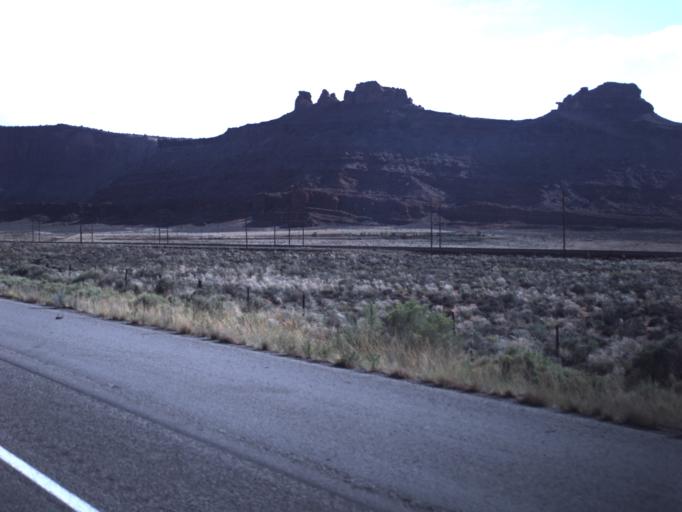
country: US
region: Utah
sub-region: Grand County
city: Moab
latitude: 38.6648
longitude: -109.6819
